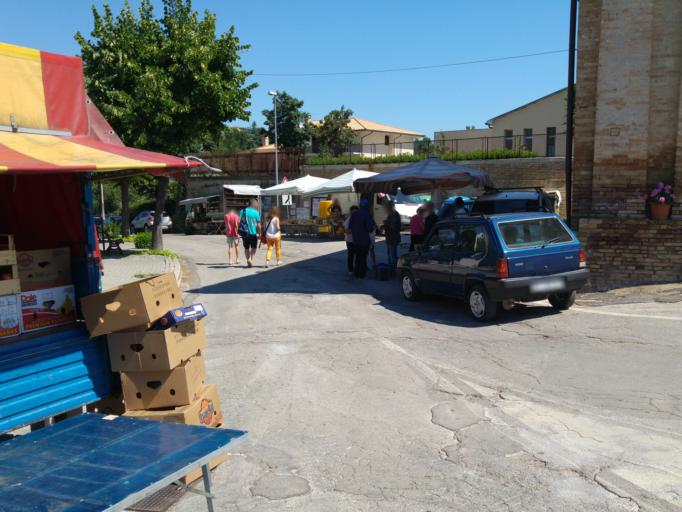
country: IT
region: Abruzzo
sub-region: Provincia di Pescara
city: Elice
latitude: 42.5215
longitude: 13.9699
